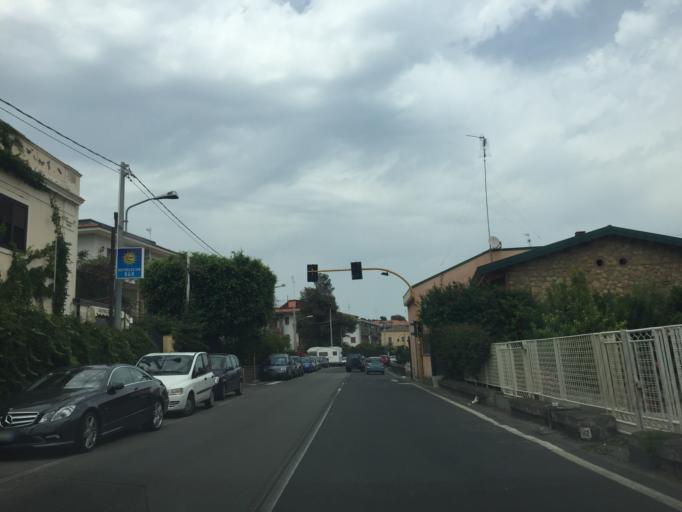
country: IT
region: Sicily
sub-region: Catania
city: Vambolieri
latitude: 37.5712
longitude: 15.1650
